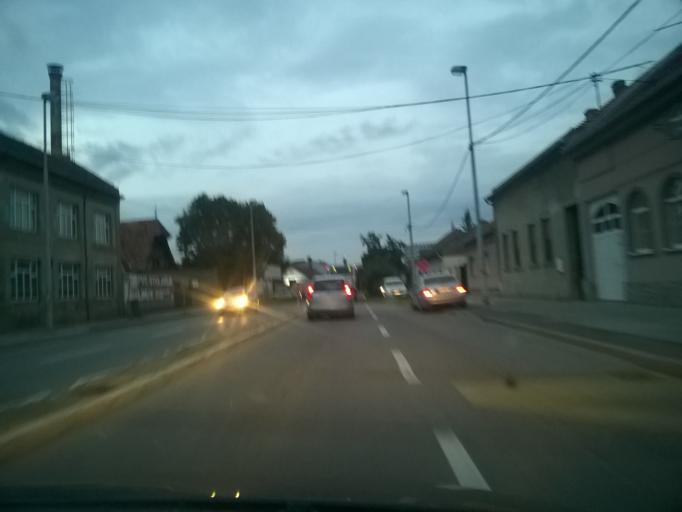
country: RS
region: Autonomna Pokrajina Vojvodina
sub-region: Juznobanatski Okrug
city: Pancevo
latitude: 44.8586
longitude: 20.6529
